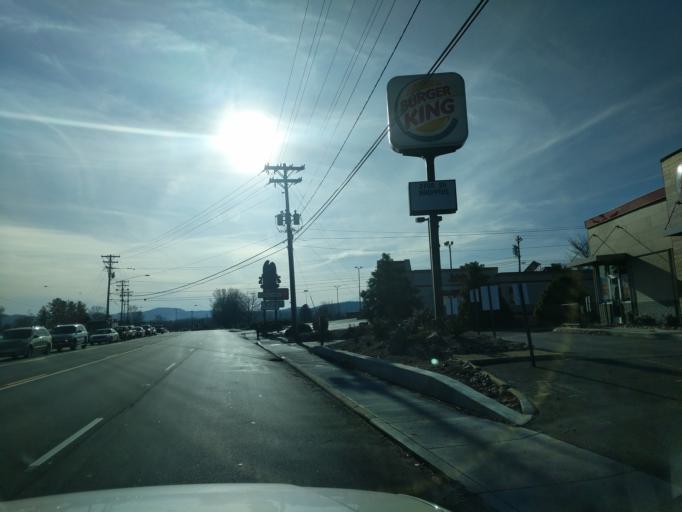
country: US
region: North Carolina
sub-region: Henderson County
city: Hendersonville
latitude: 35.3366
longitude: -82.4460
